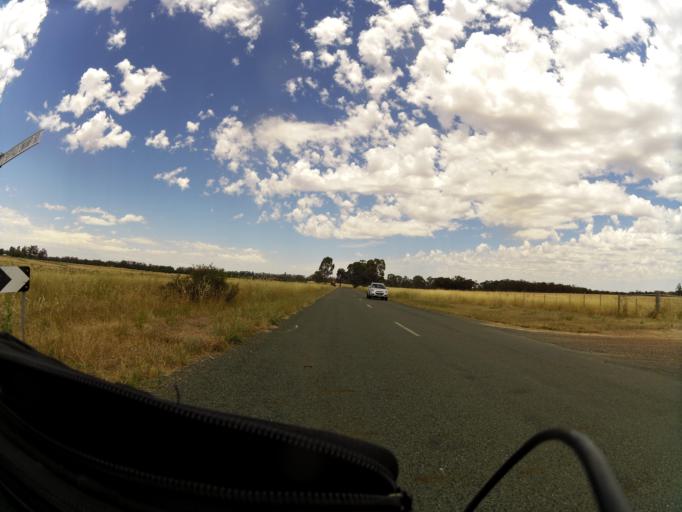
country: AU
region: Victoria
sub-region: Greater Shepparton
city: Shepparton
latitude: -36.6752
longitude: 145.1970
